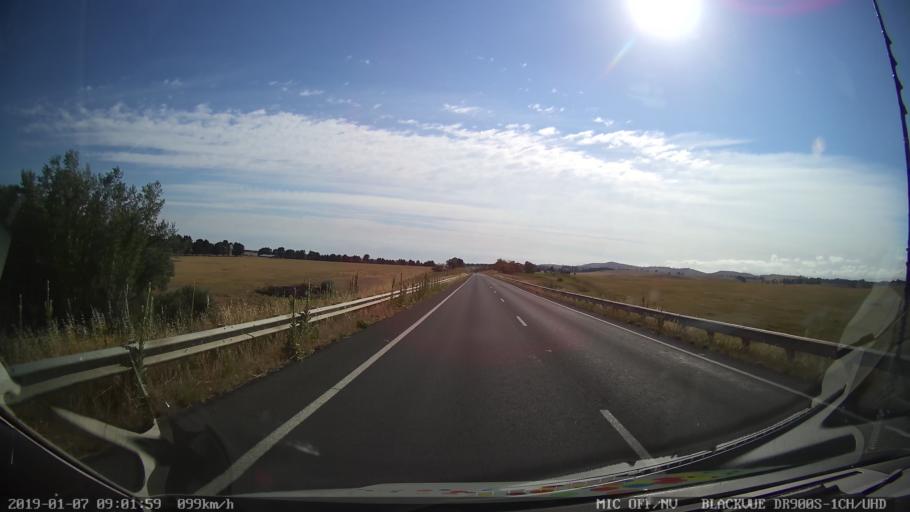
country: AU
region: New South Wales
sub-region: Armidale Dumaresq
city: Armidale
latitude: -30.7378
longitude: 151.4155
